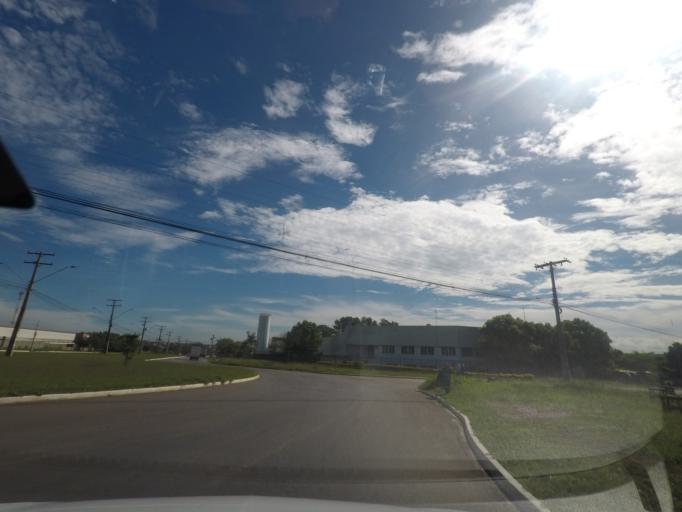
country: BR
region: Goias
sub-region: Aparecida De Goiania
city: Aparecida de Goiania
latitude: -16.7936
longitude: -49.2536
